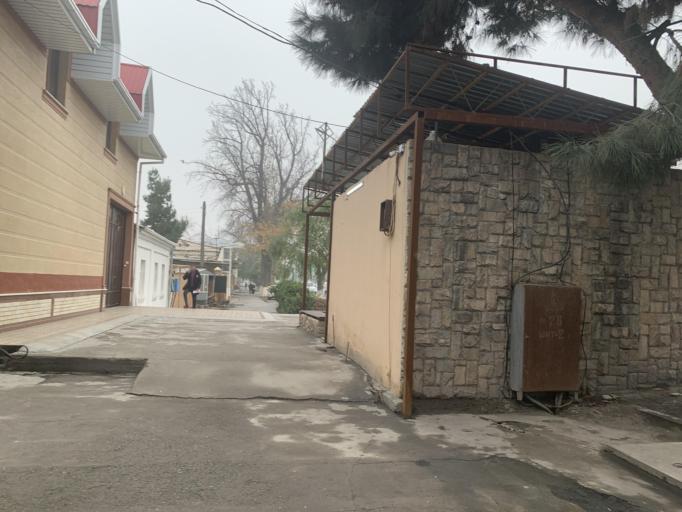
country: UZ
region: Fergana
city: Qo`qon
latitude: 40.5387
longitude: 70.9248
